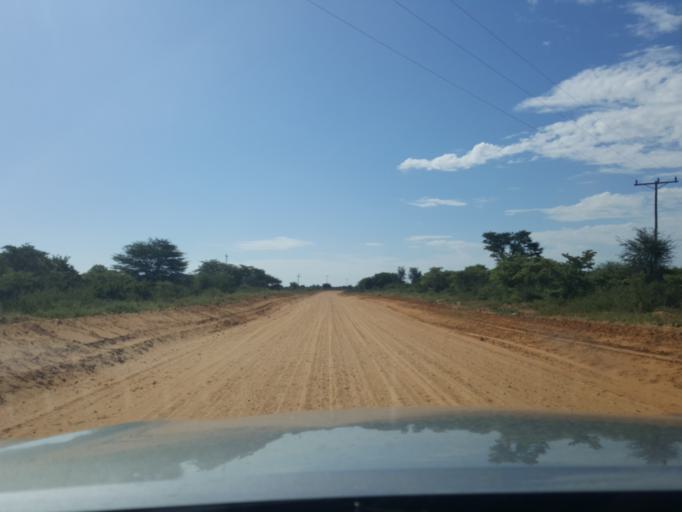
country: BW
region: Kweneng
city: Khudumelapye
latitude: -23.7035
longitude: 24.7232
